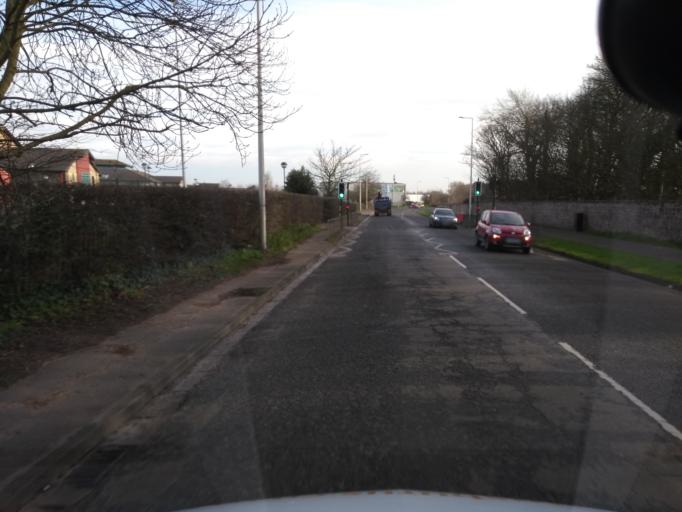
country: GB
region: England
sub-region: North Somerset
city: Weston-super-Mare
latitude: 51.3278
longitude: -2.9777
